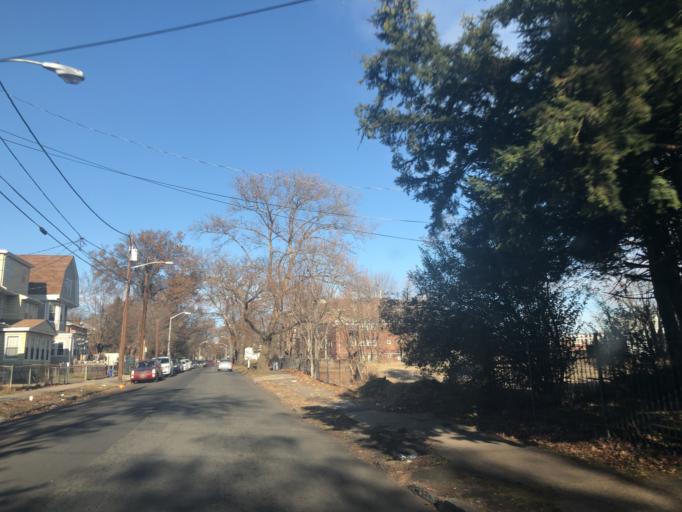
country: US
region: New Jersey
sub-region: Essex County
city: East Orange
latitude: 40.7483
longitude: -74.2159
